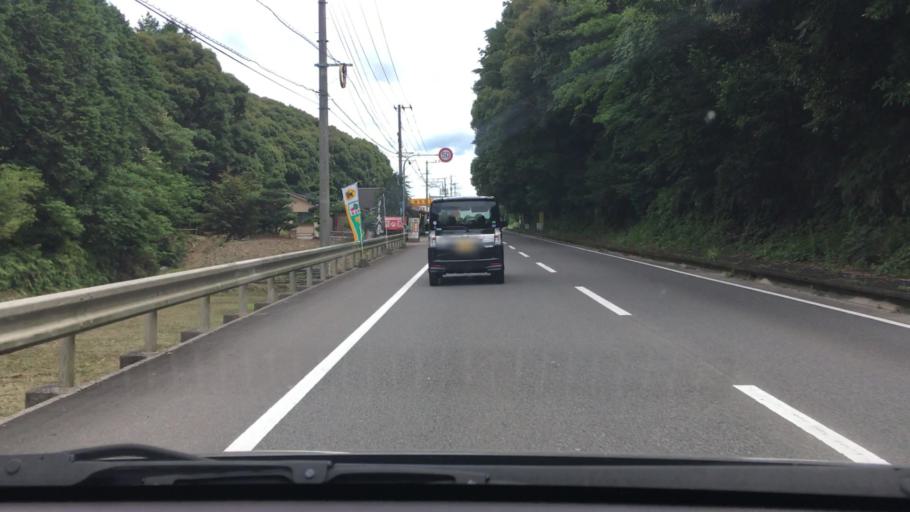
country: JP
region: Nagasaki
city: Togitsu
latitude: 32.9722
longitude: 129.7819
